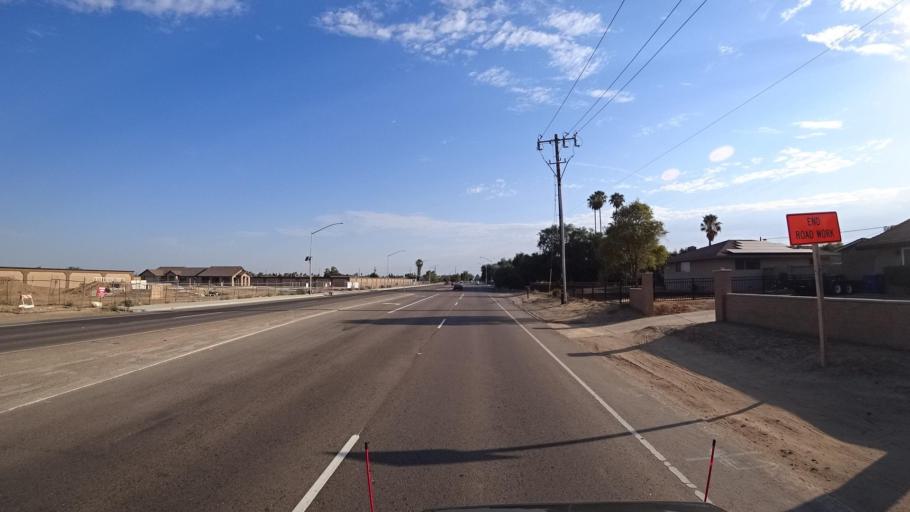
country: US
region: California
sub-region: Fresno County
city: Sunnyside
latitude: 36.7097
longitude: -119.7000
